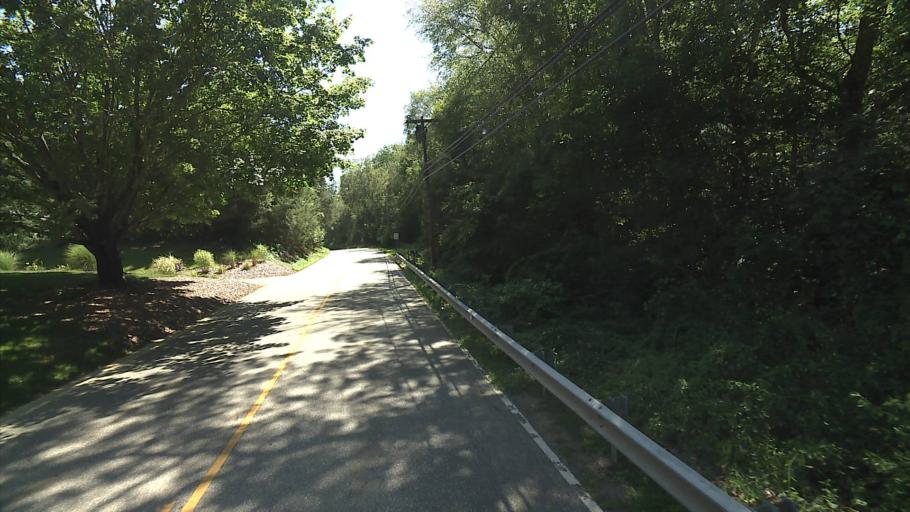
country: US
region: Connecticut
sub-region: New London County
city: Baltic
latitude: 41.6280
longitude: -72.0857
